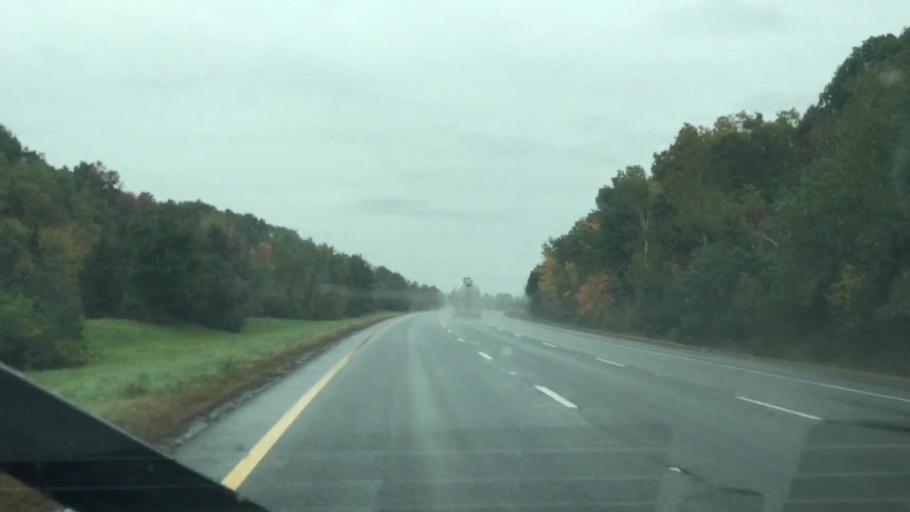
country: US
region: Massachusetts
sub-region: Essex County
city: Merrimac
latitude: 42.8161
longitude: -71.0225
